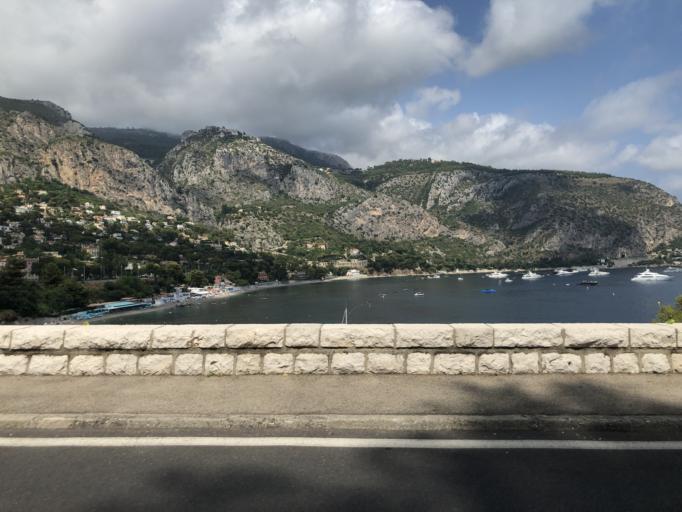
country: FR
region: Provence-Alpes-Cote d'Azur
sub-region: Departement des Alpes-Maritimes
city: Eze
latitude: 43.7162
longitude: 7.3506
